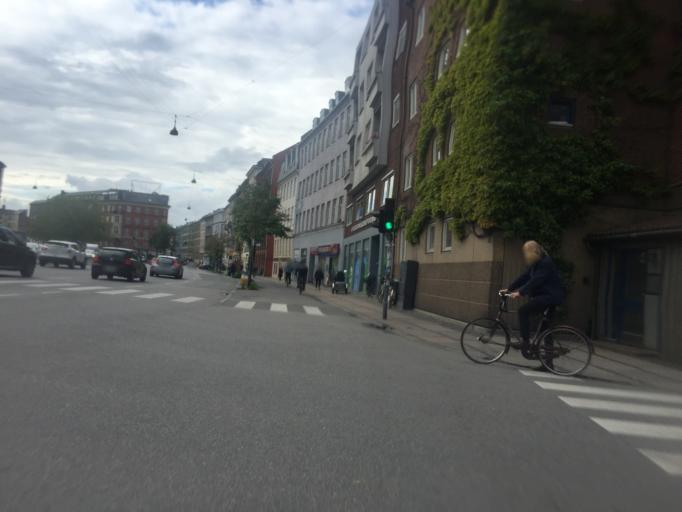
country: DK
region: Capital Region
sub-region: Kobenhavn
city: Copenhagen
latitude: 55.6842
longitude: 12.5554
